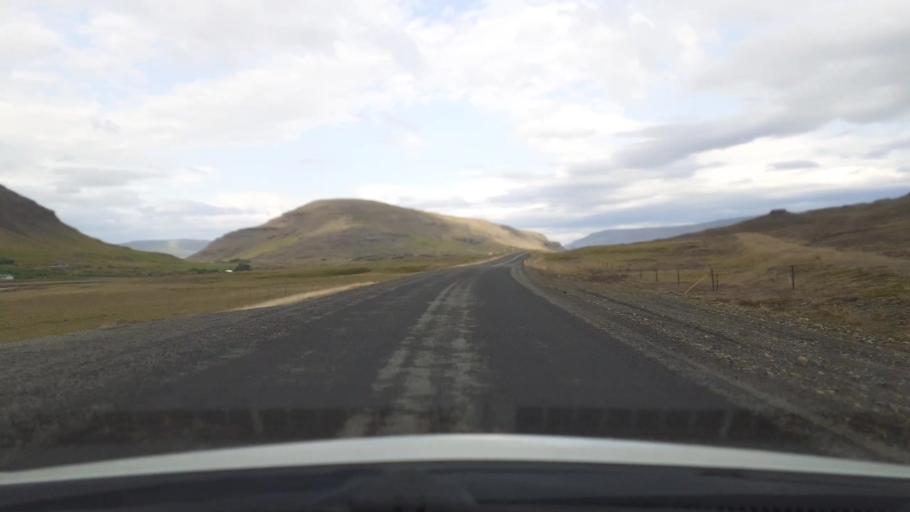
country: IS
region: Capital Region
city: Mosfellsbaer
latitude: 64.3002
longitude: -21.4814
